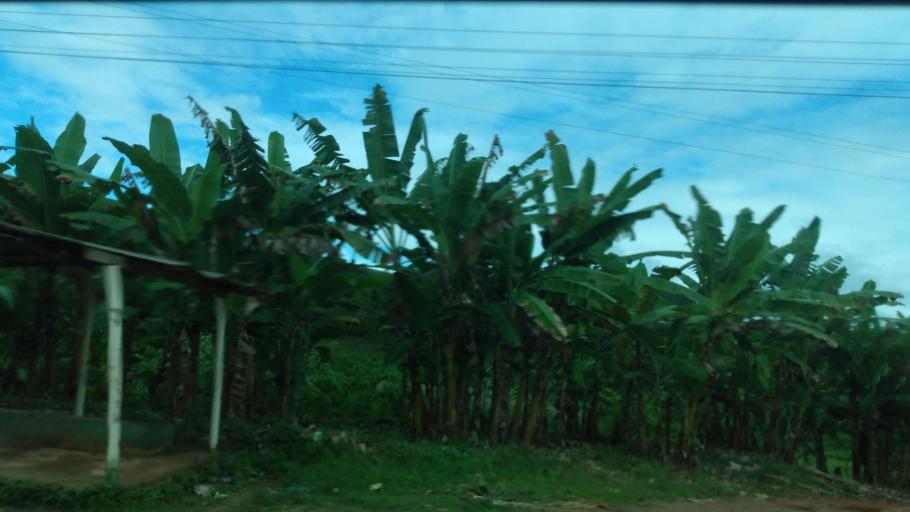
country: BR
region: Pernambuco
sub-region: Catende
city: Catende
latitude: -8.7121
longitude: -35.7710
